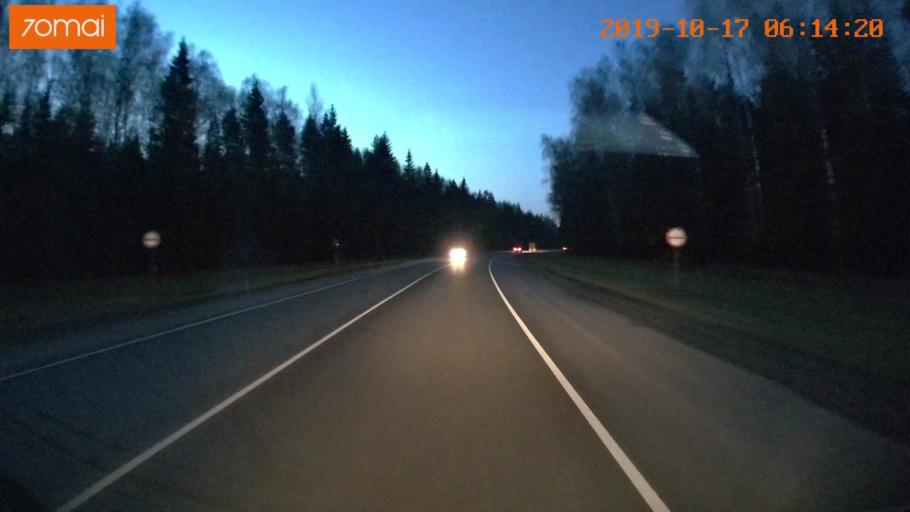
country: RU
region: Ivanovo
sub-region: Gorod Ivanovo
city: Ivanovo
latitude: 56.8871
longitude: 40.9428
